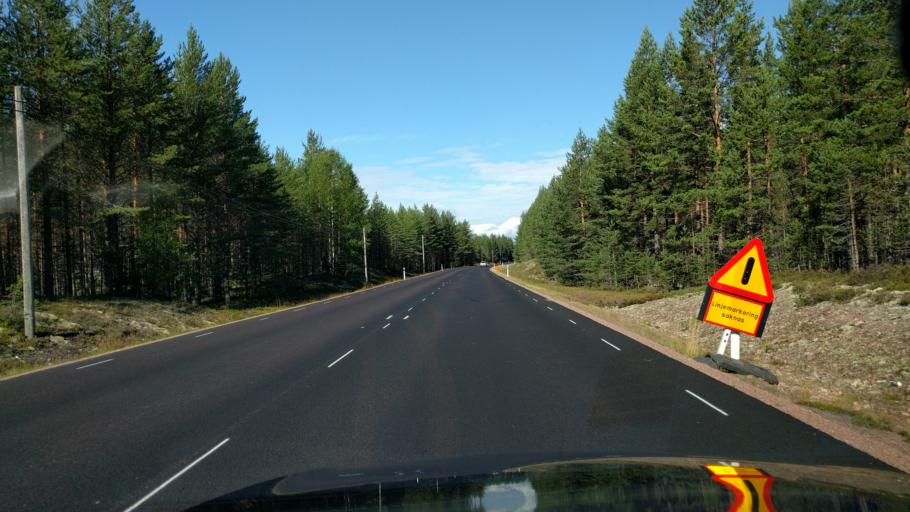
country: SE
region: Dalarna
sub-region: Alvdalens Kommun
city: AElvdalen
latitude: 61.1230
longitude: 14.2206
